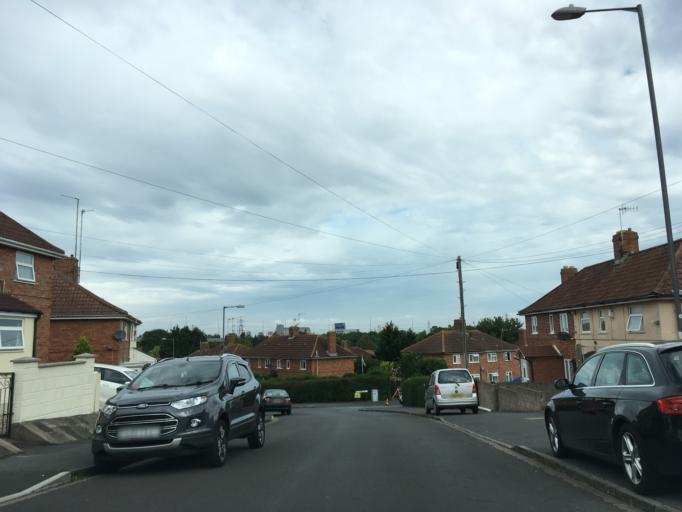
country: GB
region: England
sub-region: North Somerset
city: Easton-in-Gordano
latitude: 51.4913
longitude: -2.6836
